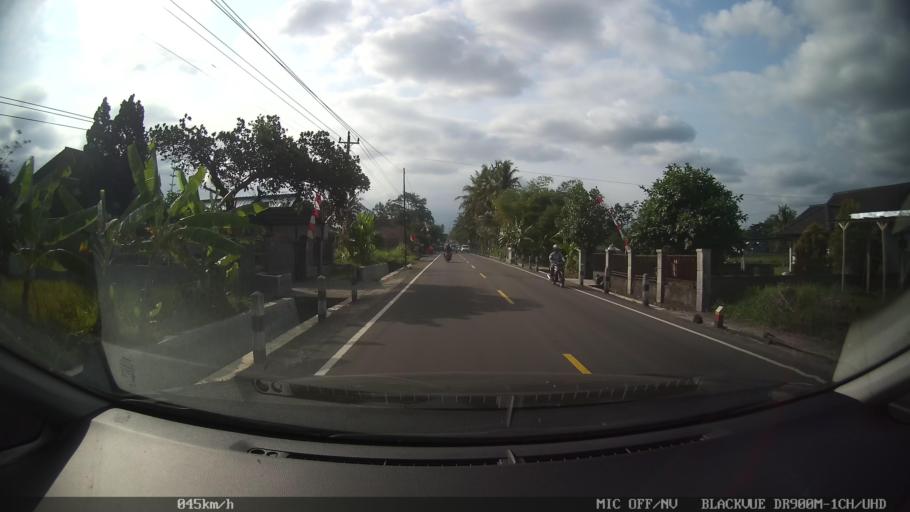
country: ID
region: Central Java
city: Candi Prambanan
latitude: -7.6951
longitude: 110.4638
